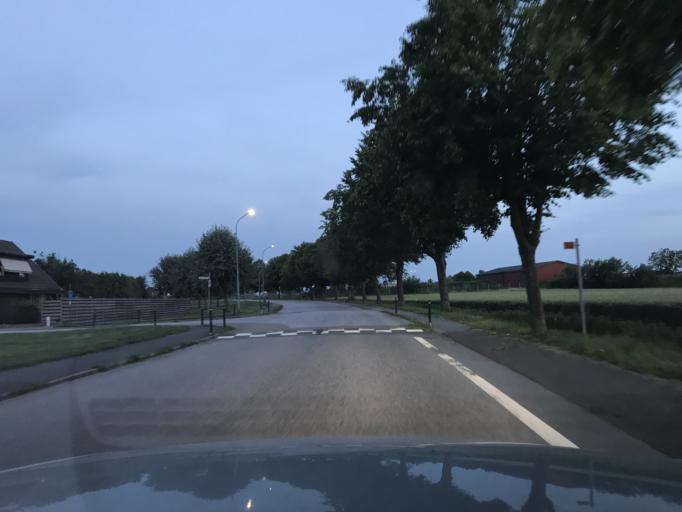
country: SE
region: Skane
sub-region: Svalovs Kommun
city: Svaloev
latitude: 55.9101
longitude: 13.0921
